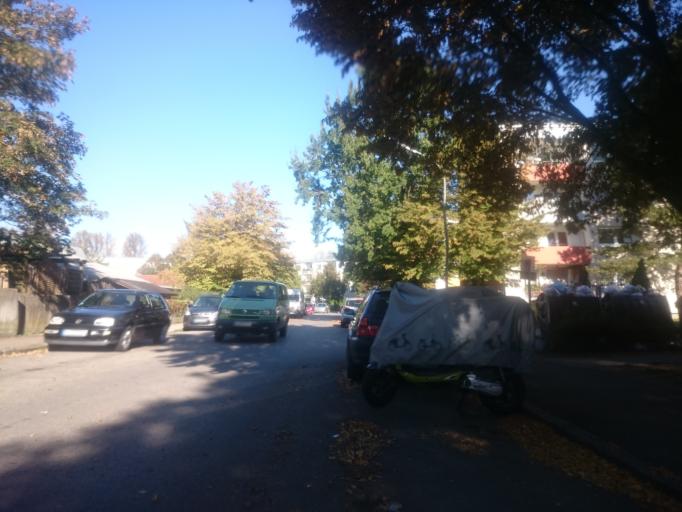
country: DE
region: Bavaria
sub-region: Swabia
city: Augsburg
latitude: 48.3714
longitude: 10.9275
